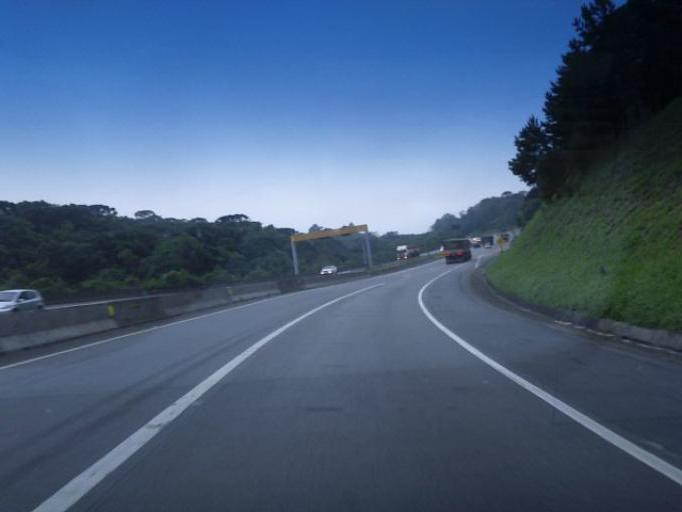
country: BR
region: Parana
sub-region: Sao Jose Dos Pinhais
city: Sao Jose dos Pinhais
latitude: -25.8449
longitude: -49.0738
